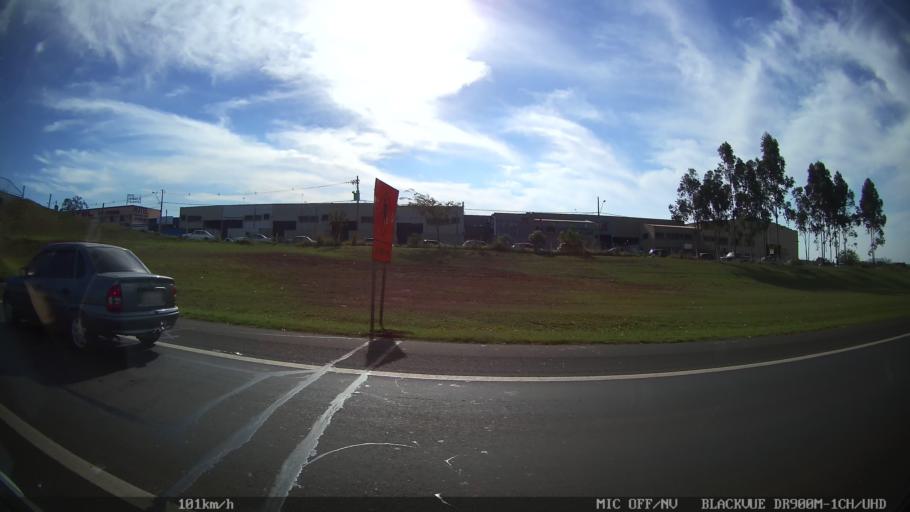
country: BR
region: Sao Paulo
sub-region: Araraquara
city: Araraquara
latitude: -21.7970
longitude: -48.1385
